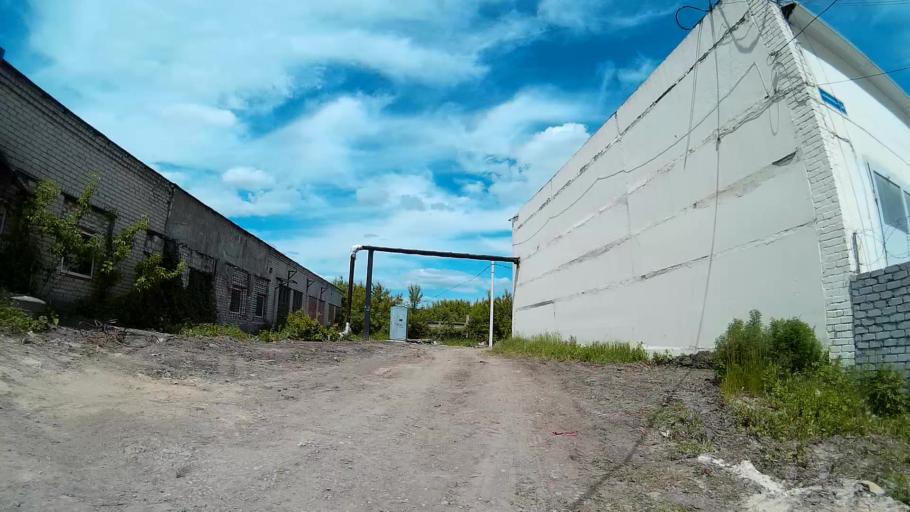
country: RU
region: Ulyanovsk
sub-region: Ulyanovskiy Rayon
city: Ulyanovsk
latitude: 54.2787
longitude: 48.3531
